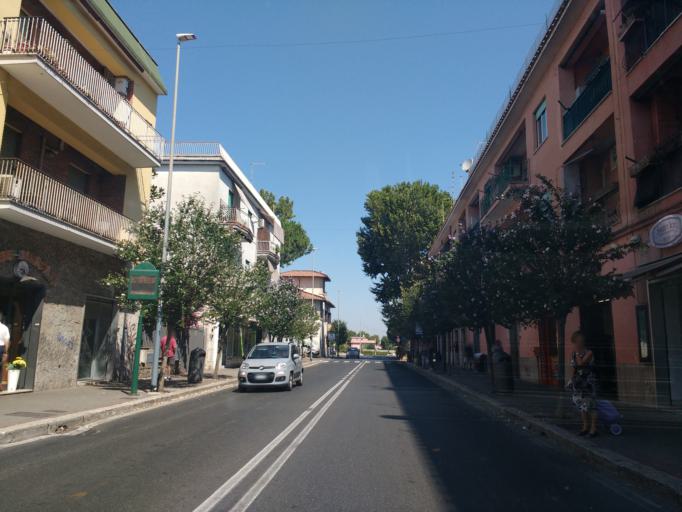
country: IT
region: Latium
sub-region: Citta metropolitana di Roma Capitale
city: Acilia-Castel Fusano-Ostia Antica
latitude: 41.7837
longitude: 12.3649
